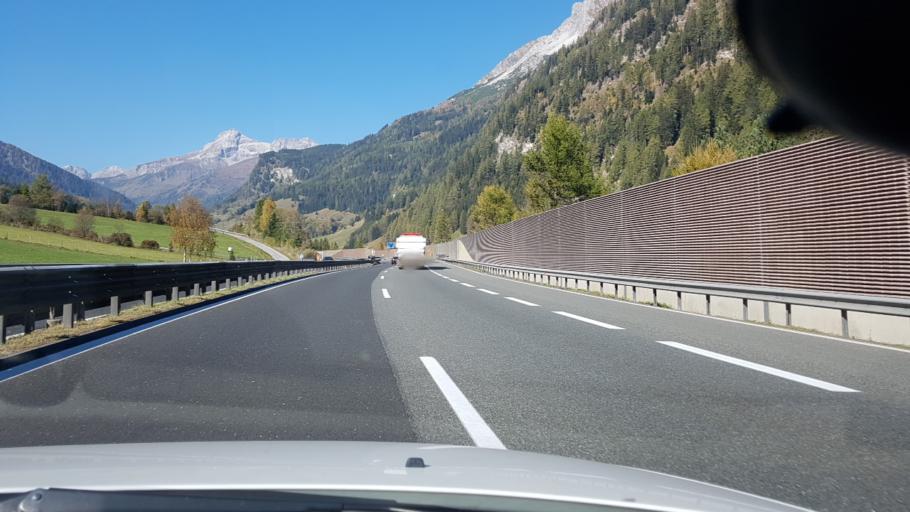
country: AT
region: Salzburg
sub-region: Politischer Bezirk Tamsweg
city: Zederhaus
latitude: 47.1601
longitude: 13.4833
